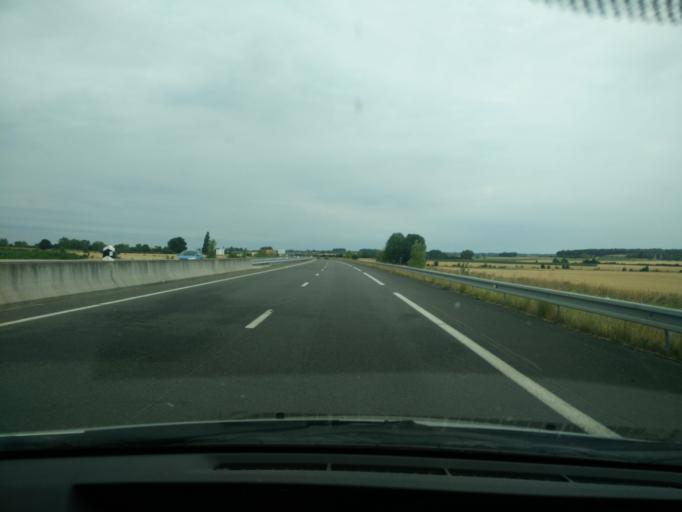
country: FR
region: Pays de la Loire
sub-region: Departement de Maine-et-Loire
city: Saint-Jean
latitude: 47.2633
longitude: -0.3343
